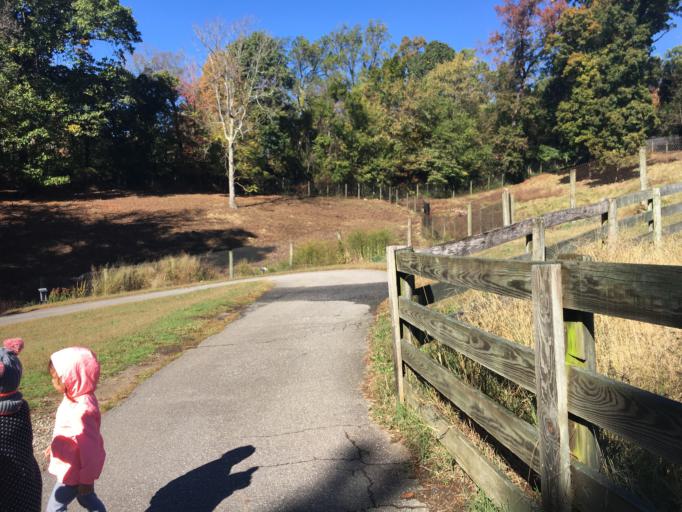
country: US
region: Virginia
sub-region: City of Richmond
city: Richmond
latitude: 37.5365
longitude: -77.4806
